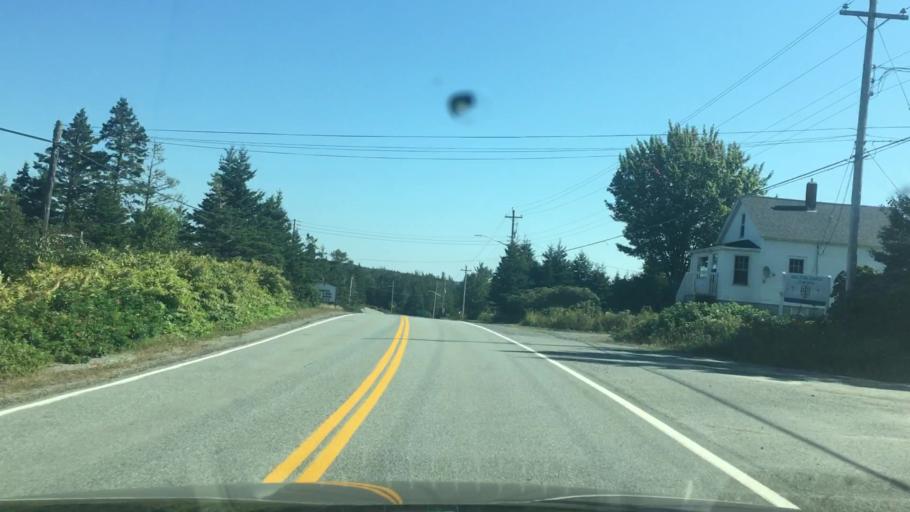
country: CA
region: Nova Scotia
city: New Glasgow
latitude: 44.8038
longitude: -62.6964
